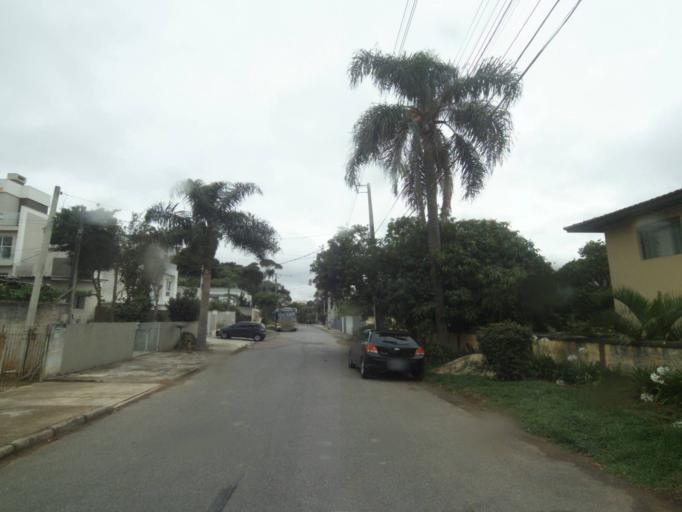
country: BR
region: Parana
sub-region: Curitiba
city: Curitiba
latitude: -25.4284
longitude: -49.3371
